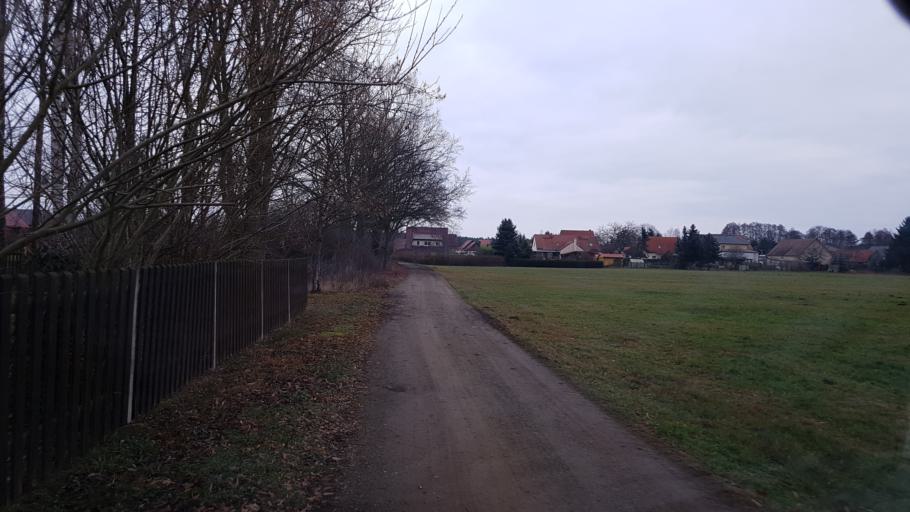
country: DE
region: Brandenburg
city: Doberlug-Kirchhain
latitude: 51.6094
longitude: 13.5944
